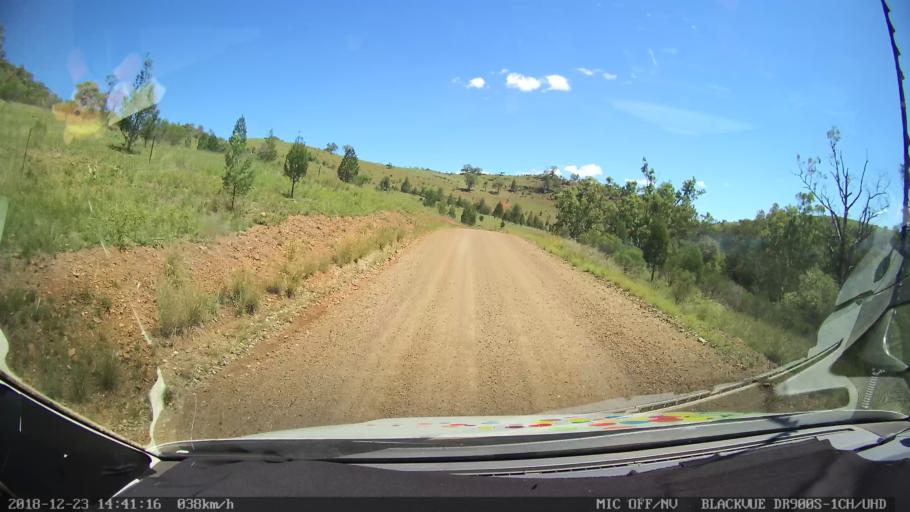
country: AU
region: New South Wales
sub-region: Tamworth Municipality
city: Manilla
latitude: -30.6304
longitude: 150.9025
